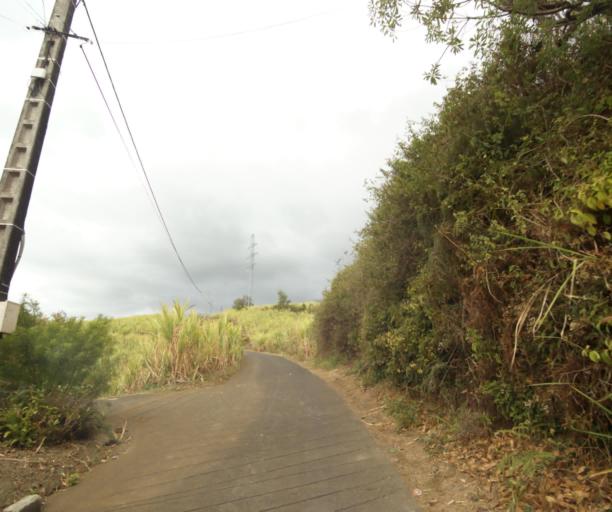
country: RE
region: Reunion
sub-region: Reunion
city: Saint-Paul
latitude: -21.0303
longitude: 55.3153
